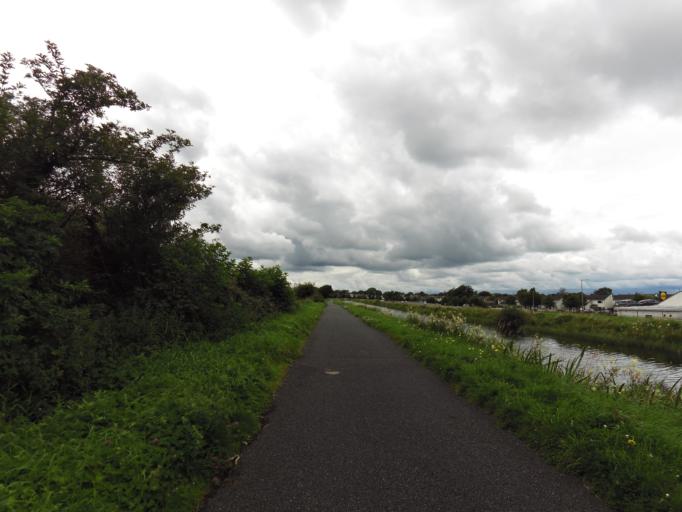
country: IE
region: Leinster
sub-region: An Iarmhi
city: An Muileann gCearr
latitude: 53.5200
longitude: -7.3591
